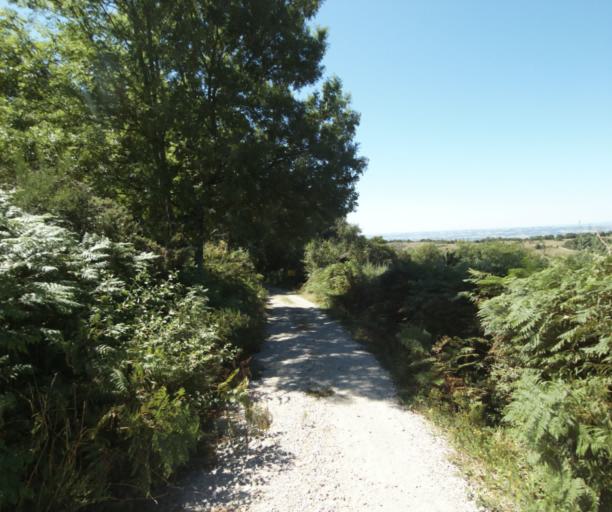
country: FR
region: Midi-Pyrenees
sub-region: Departement du Tarn
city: Soreze
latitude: 43.4423
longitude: 2.0978
